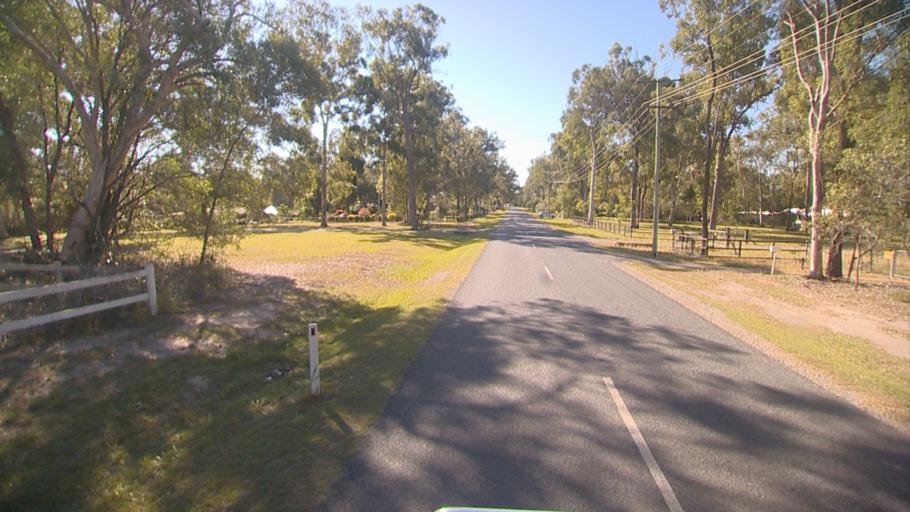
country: AU
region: Queensland
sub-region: Logan
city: Logan Reserve
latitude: -27.7344
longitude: 153.1229
